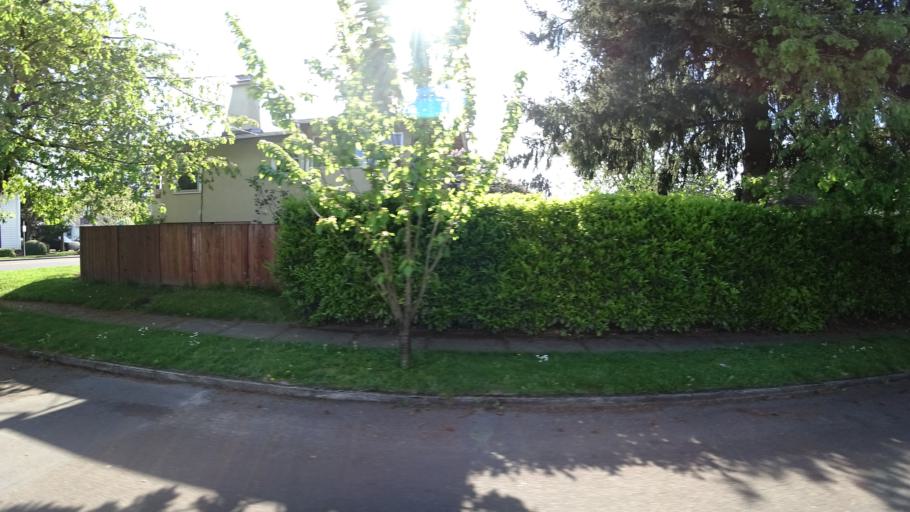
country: US
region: Oregon
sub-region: Clackamas County
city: Milwaukie
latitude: 45.4467
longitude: -122.6335
